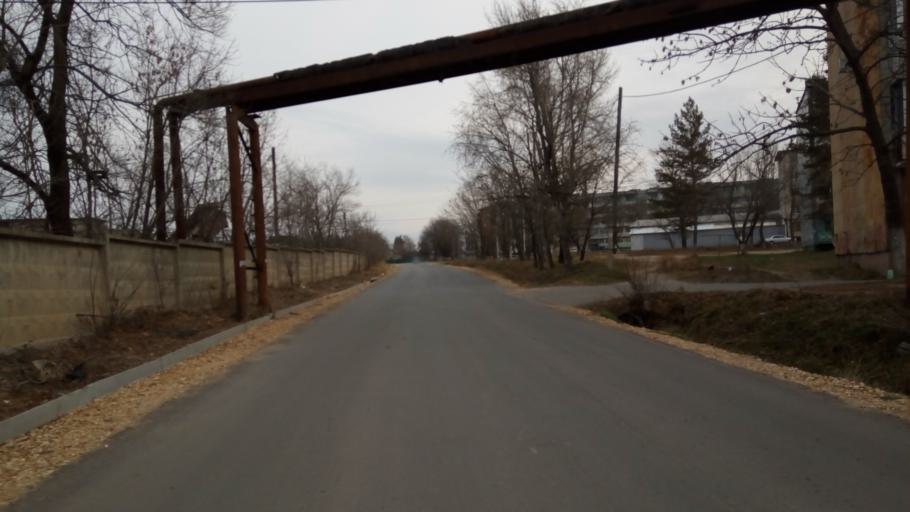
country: RU
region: Primorskiy
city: Novoshakhtinskiy
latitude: 44.0297
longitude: 132.1700
